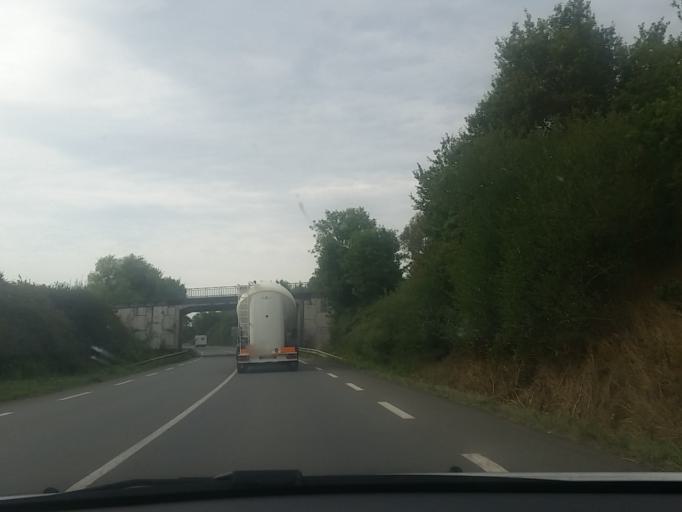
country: FR
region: Pays de la Loire
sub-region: Departement de la Vendee
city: Chantonnay
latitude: 46.6864
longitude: -1.0662
